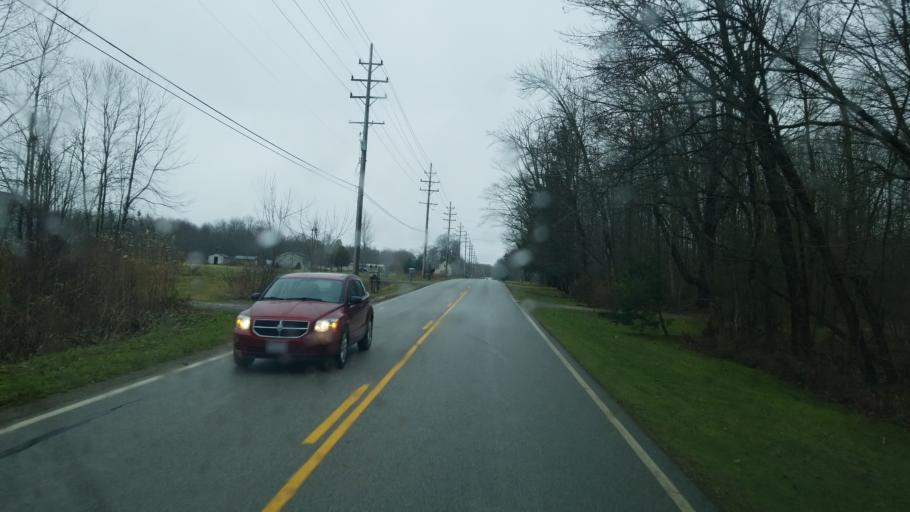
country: US
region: Ohio
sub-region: Ashtabula County
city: Jefferson
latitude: 41.7699
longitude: -80.8098
